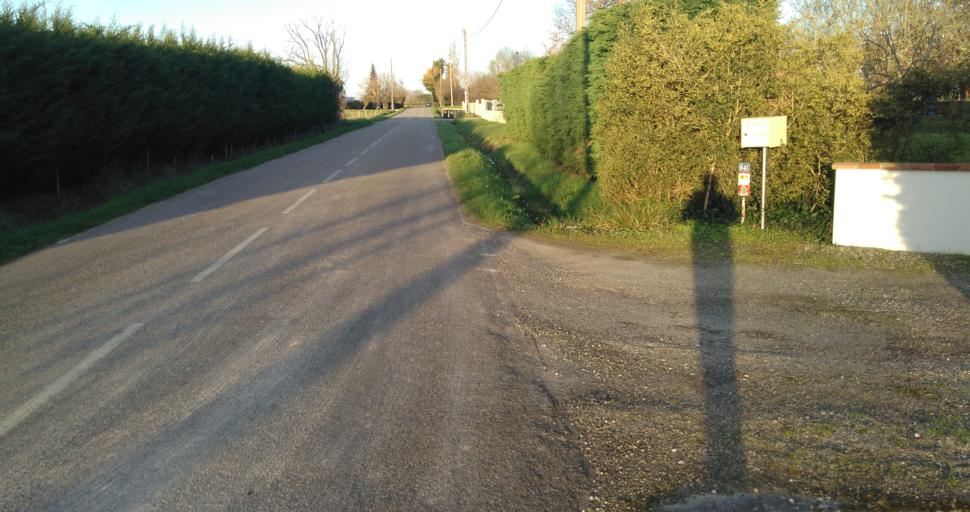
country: FR
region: Midi-Pyrenees
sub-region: Departement du Tarn-et-Garonne
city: Montech
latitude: 43.9836
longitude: 1.2547
